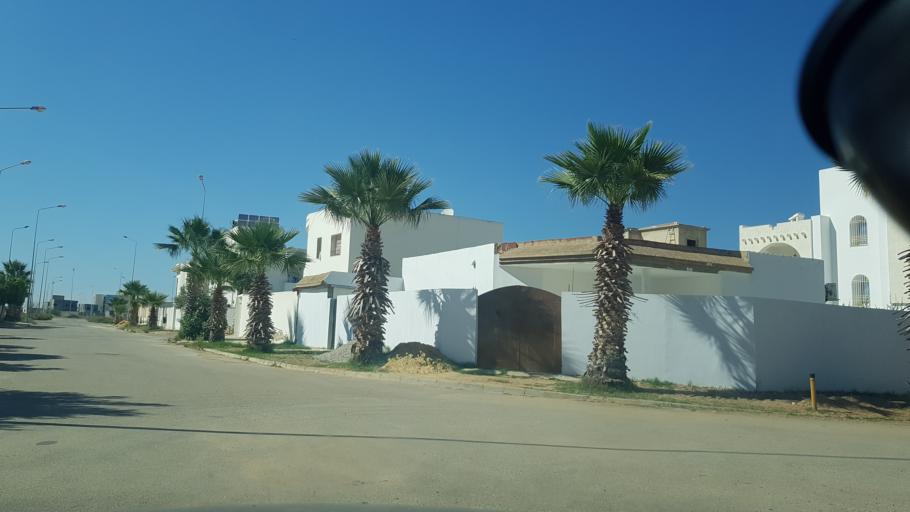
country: TN
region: Safaqis
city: Al Qarmadah
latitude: 34.8293
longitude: 10.7557
